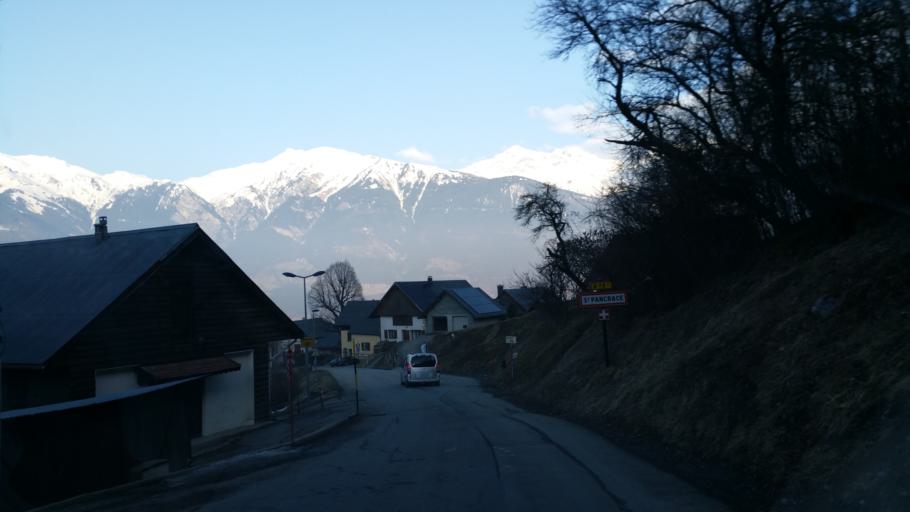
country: FR
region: Rhone-Alpes
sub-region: Departement de la Savoie
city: Saint-Jean-de-Maurienne
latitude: 45.2683
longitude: 6.3234
